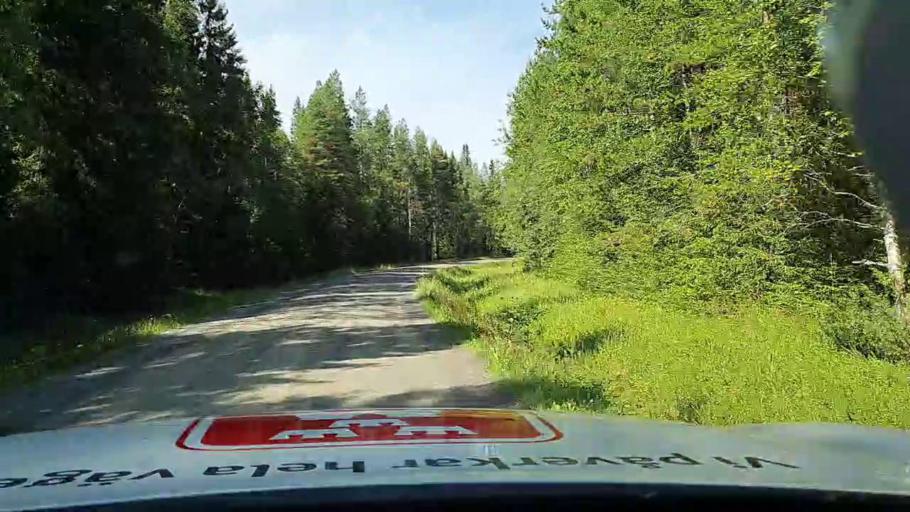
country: SE
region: Jaemtland
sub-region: Stroemsunds Kommun
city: Stroemsund
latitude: 63.7309
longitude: 15.2477
